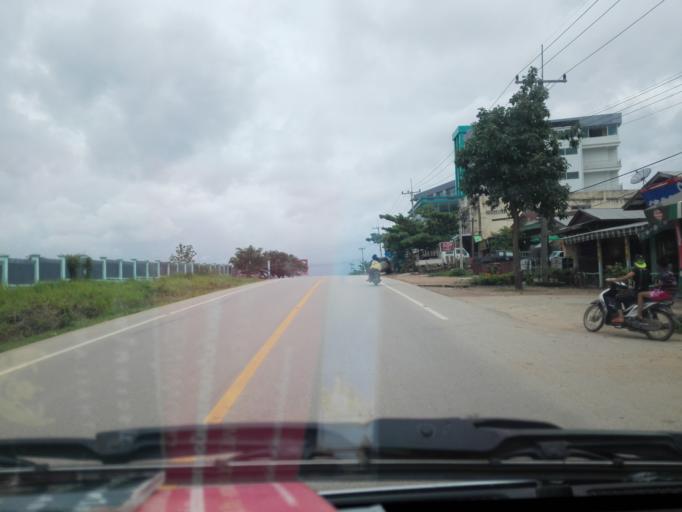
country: TH
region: Tak
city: Mae Sot
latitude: 16.6854
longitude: 98.4820
